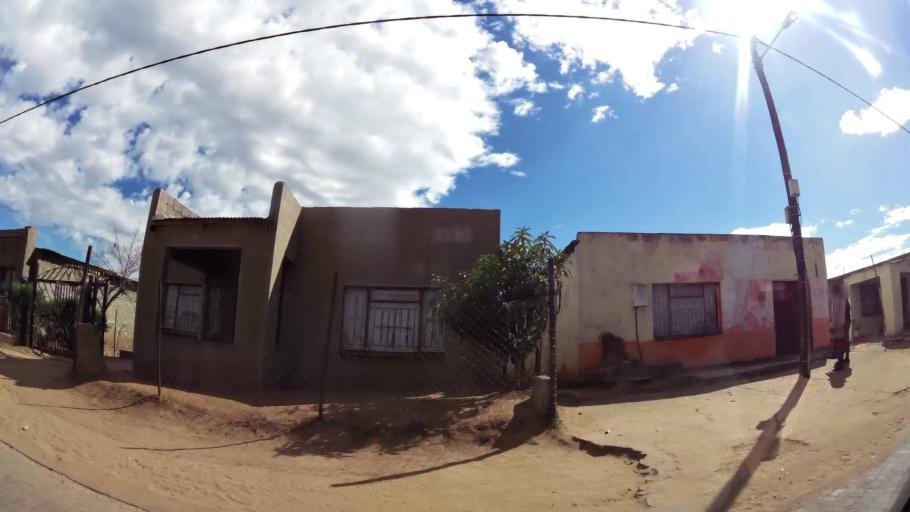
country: ZA
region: Limpopo
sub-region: Waterberg District Municipality
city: Bela-Bela
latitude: -24.8832
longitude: 28.3122
